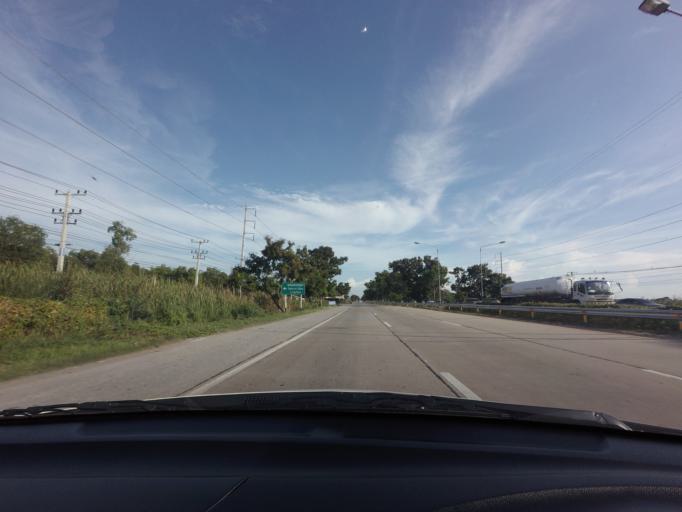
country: TH
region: Phra Nakhon Si Ayutthaya
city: Lat Bua Luang
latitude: 14.1849
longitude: 100.2923
